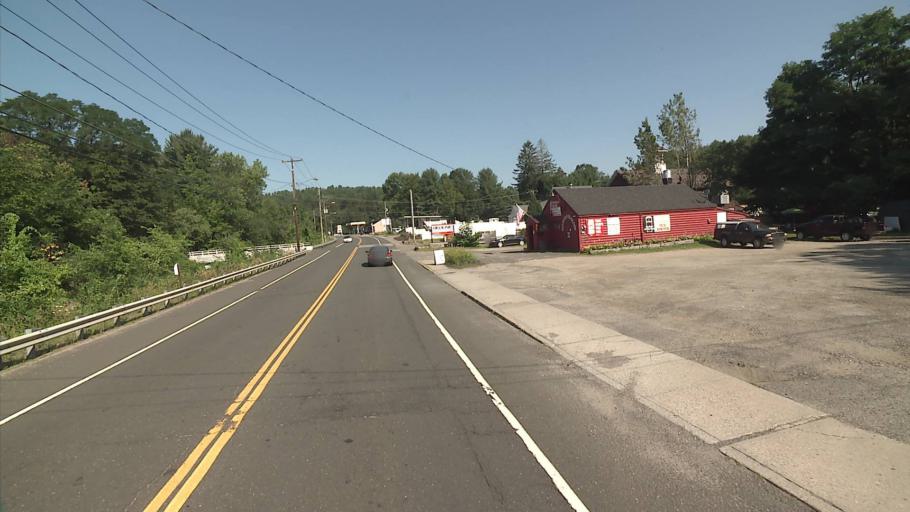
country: US
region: Connecticut
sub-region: Litchfield County
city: Winsted
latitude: 41.9302
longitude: -73.0792
